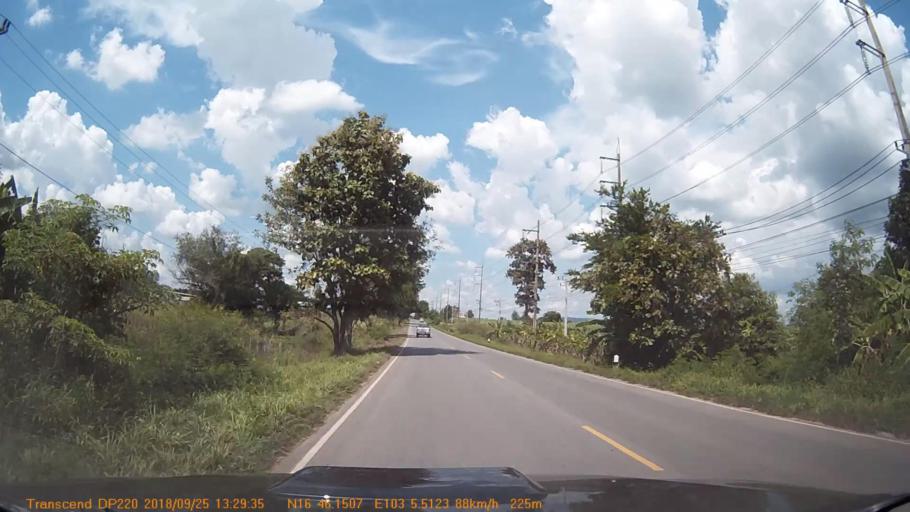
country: TH
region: Khon Kaen
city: Kranuan
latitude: 16.7691
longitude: 103.0918
